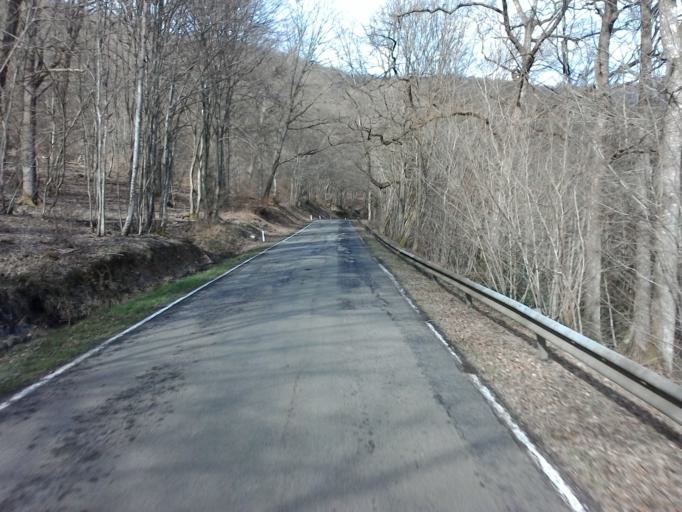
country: BE
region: Wallonia
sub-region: Province du Luxembourg
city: Daverdisse
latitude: 50.0378
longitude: 5.1245
